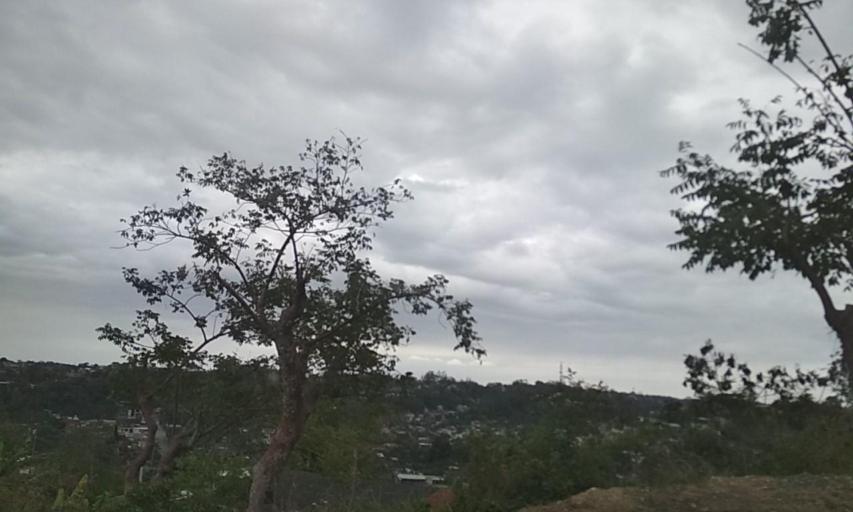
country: MX
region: Veracruz
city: Papantla de Olarte
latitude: 20.4585
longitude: -97.3170
